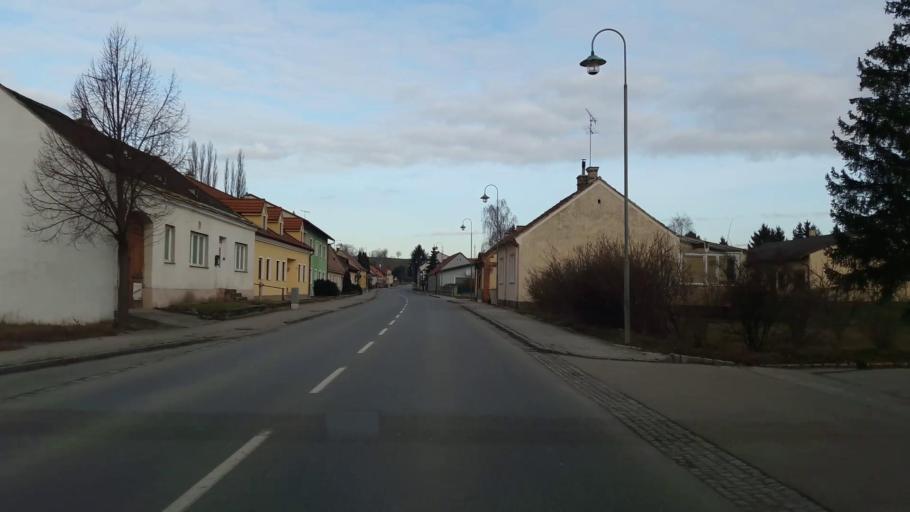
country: AT
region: Lower Austria
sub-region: Politischer Bezirk Mistelbach
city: Asparn an der Zaya
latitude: 48.6280
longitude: 16.5182
